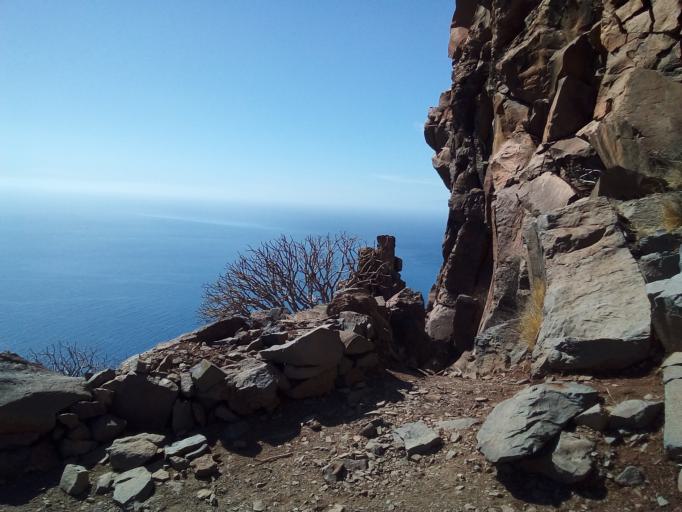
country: ES
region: Canary Islands
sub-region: Provincia de Santa Cruz de Tenerife
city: Alajero
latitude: 28.1008
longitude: -17.3373
